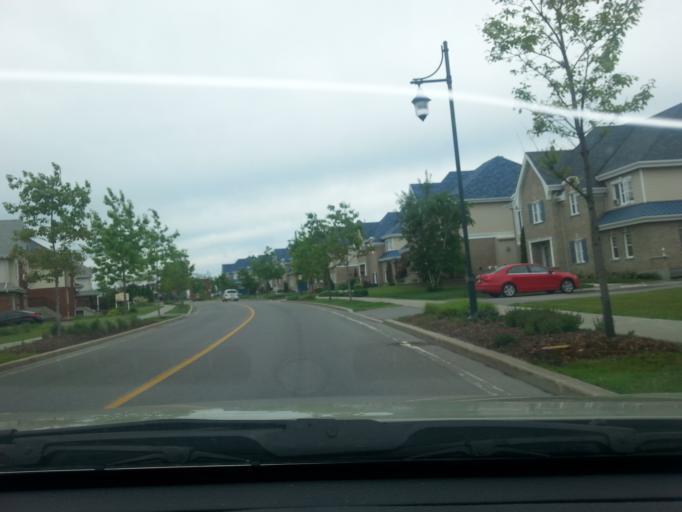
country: CA
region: Quebec
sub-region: Lanaudiere
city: Terrebonne
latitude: 45.6960
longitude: -73.6131
